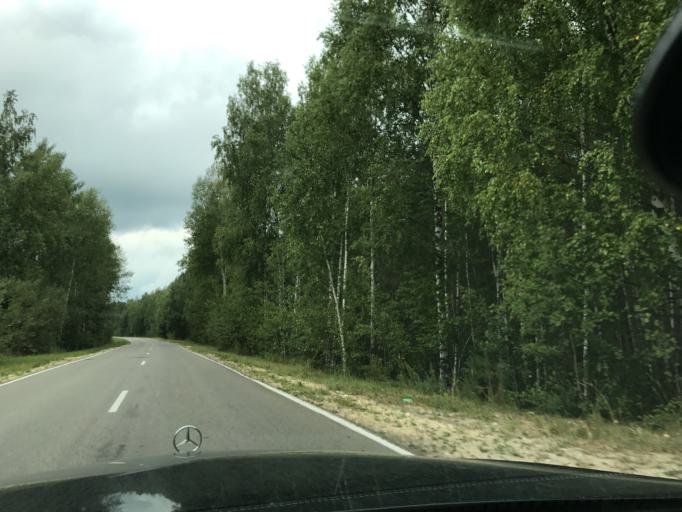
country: RU
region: Nizjnij Novgorod
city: Taremskoye
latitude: 56.0147
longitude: 42.9465
